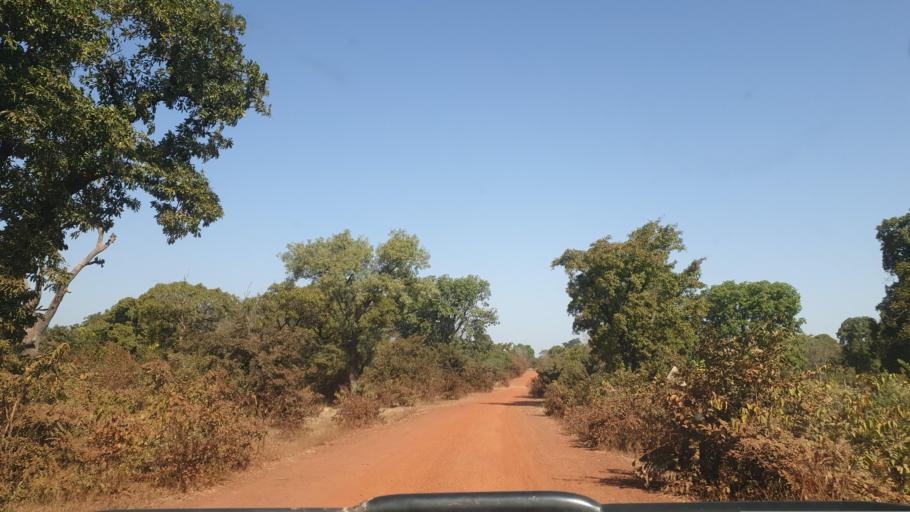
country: ML
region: Sikasso
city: Bougouni
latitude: 11.8385
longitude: -6.9783
